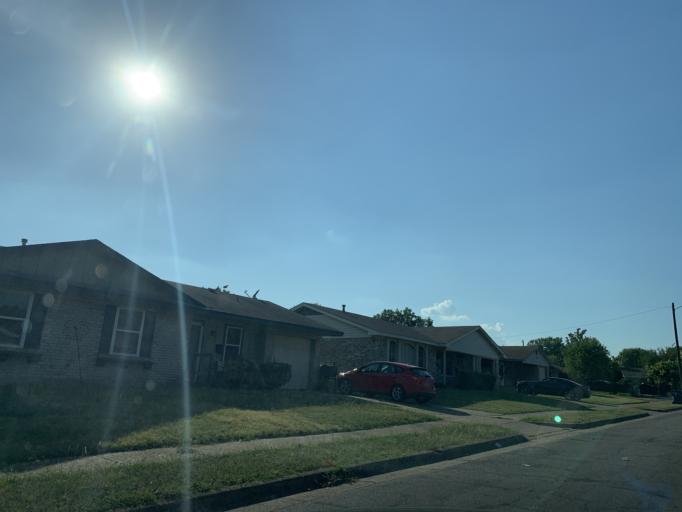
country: US
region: Texas
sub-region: Dallas County
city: Hutchins
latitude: 32.6615
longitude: -96.7616
